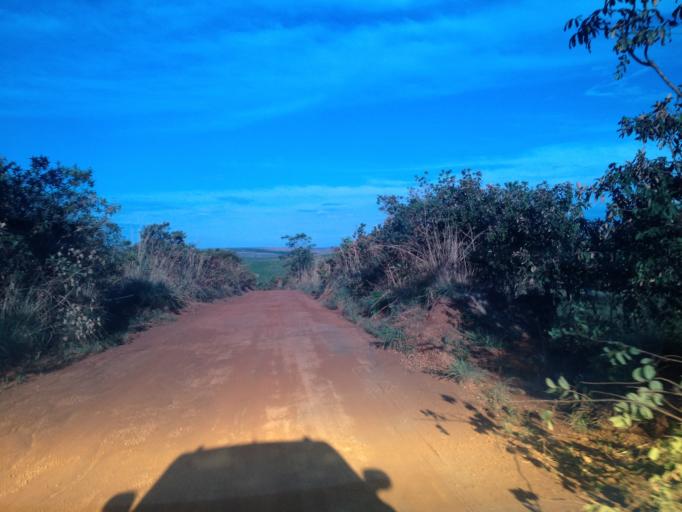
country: BR
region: Goias
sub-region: Abadiania
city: Abadiania
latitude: -15.9998
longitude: -48.5511
